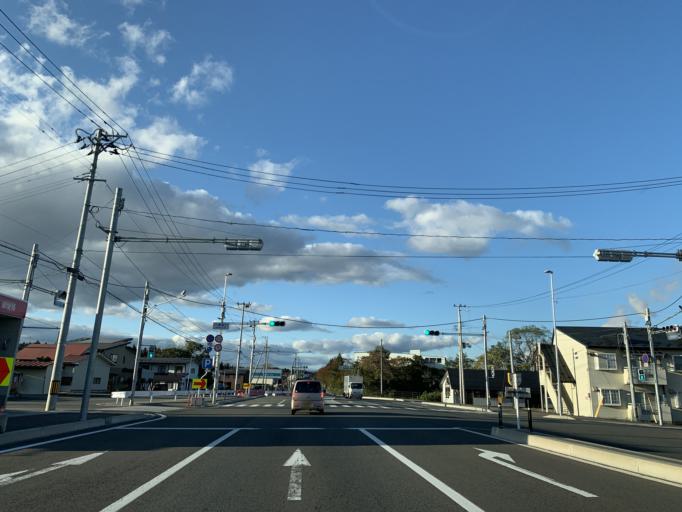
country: JP
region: Iwate
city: Kitakami
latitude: 39.2269
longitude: 141.0943
